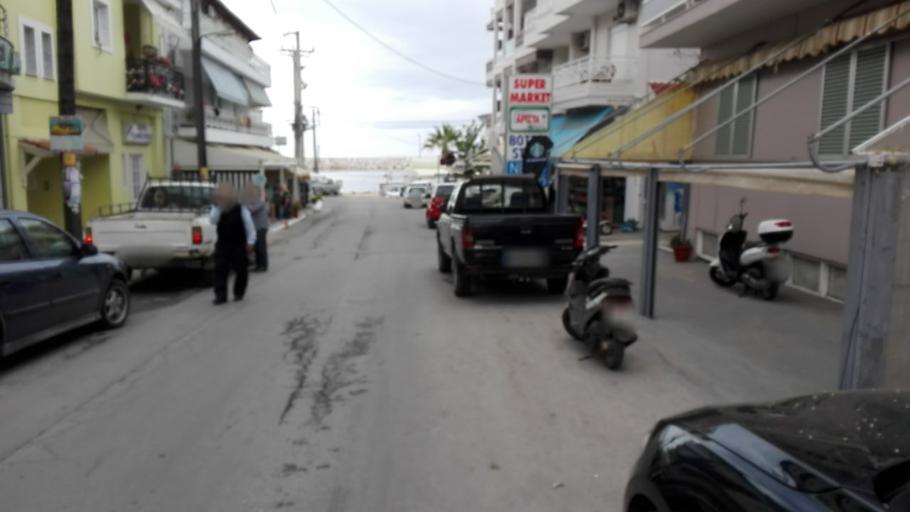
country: GR
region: East Macedonia and Thrace
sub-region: Nomos Kavalas
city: Limenaria
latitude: 40.6269
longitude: 24.5747
